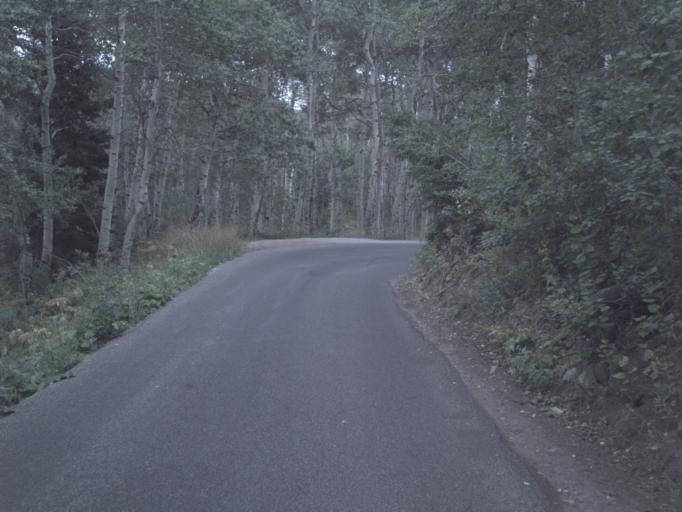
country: US
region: Utah
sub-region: Utah County
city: Lindon
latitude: 40.4248
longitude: -111.6064
